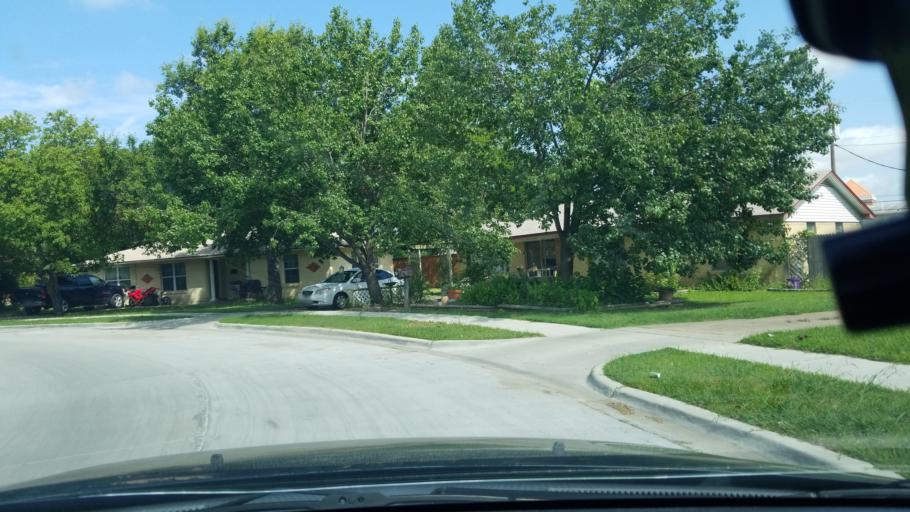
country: US
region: Texas
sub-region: Dallas County
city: Mesquite
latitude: 32.8208
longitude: -96.6479
